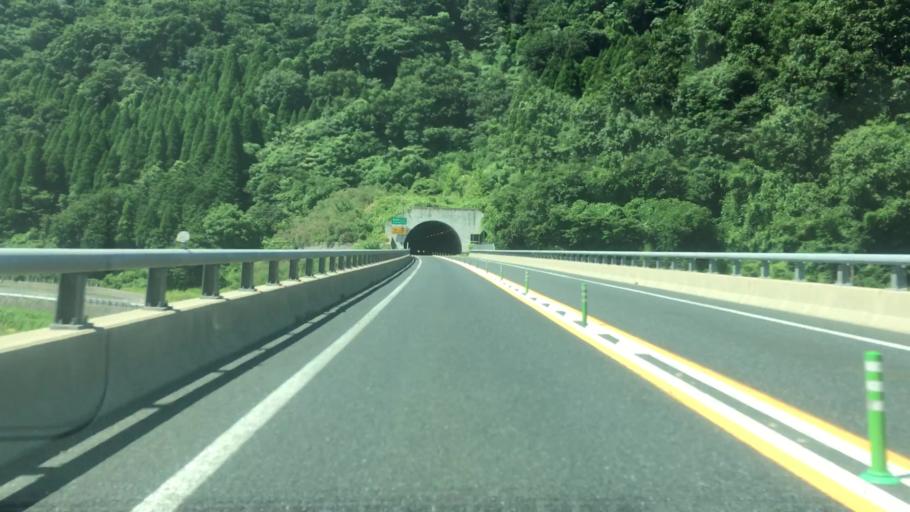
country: JP
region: Tottori
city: Tottori
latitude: 35.3799
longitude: 134.2049
